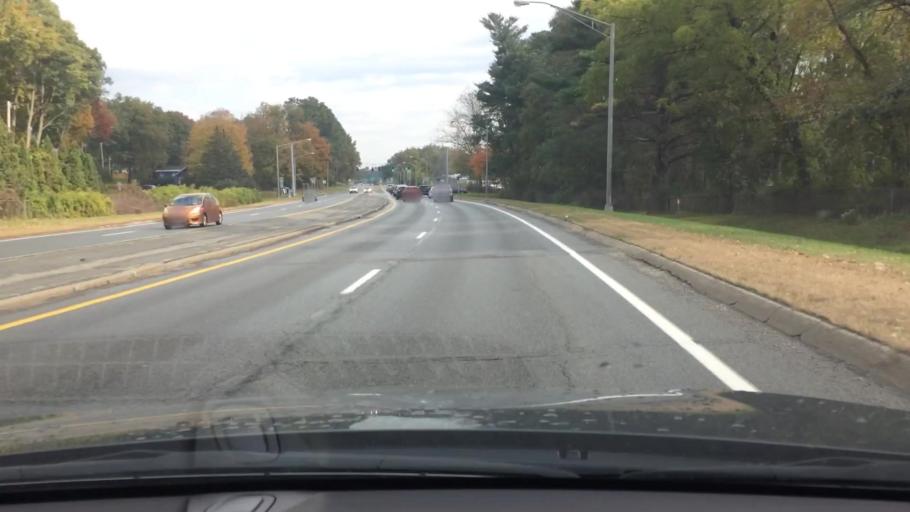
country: US
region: New York
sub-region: Saratoga County
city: Saratoga Springs
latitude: 43.0921
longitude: -73.7649
